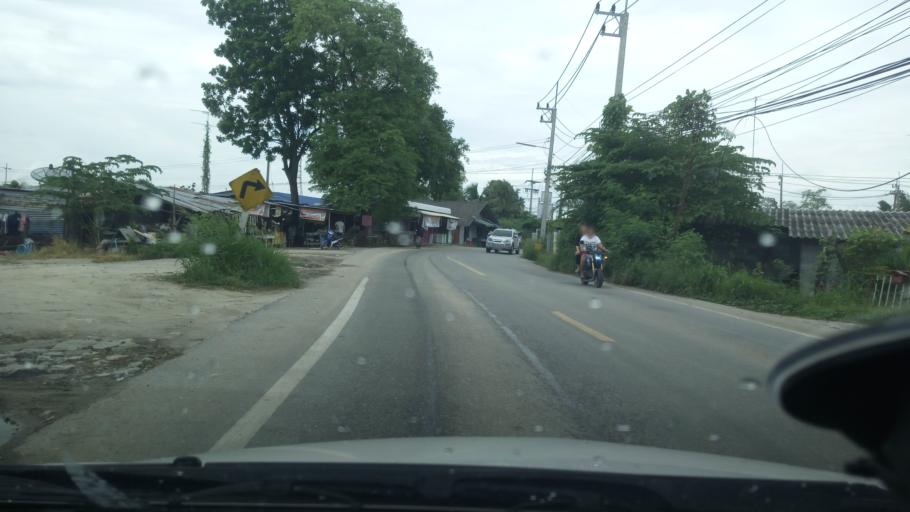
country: TH
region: Chon Buri
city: Ban Bueng
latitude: 13.3430
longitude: 101.0662
